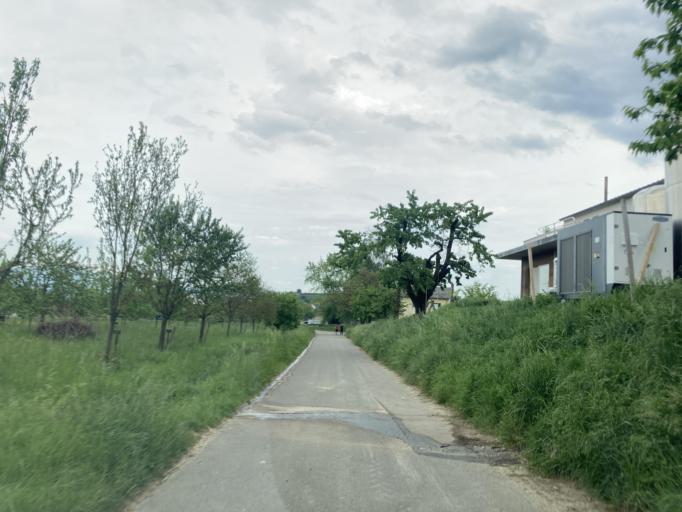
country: DE
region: Baden-Wuerttemberg
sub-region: Freiburg Region
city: Botzingen
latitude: 48.0951
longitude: 7.7209
